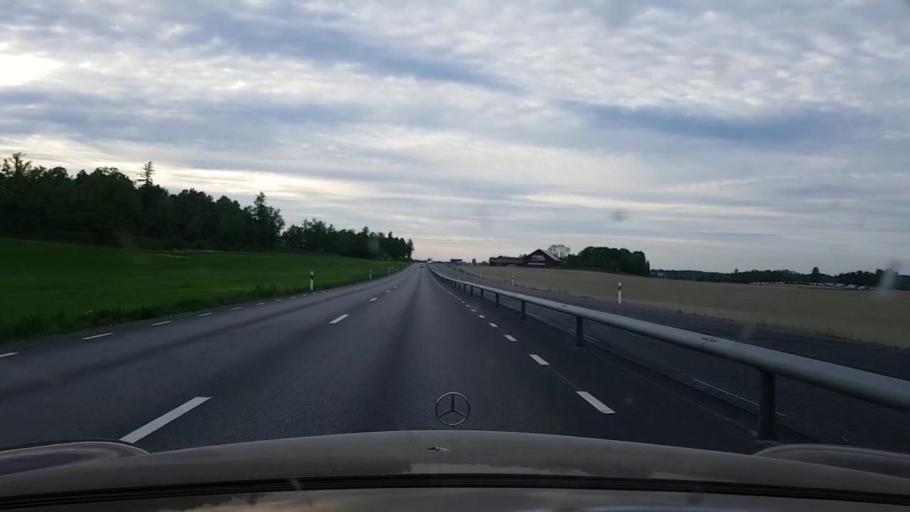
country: SE
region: OErebro
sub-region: Askersunds Kommun
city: Askersund
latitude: 58.8591
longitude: 14.9045
